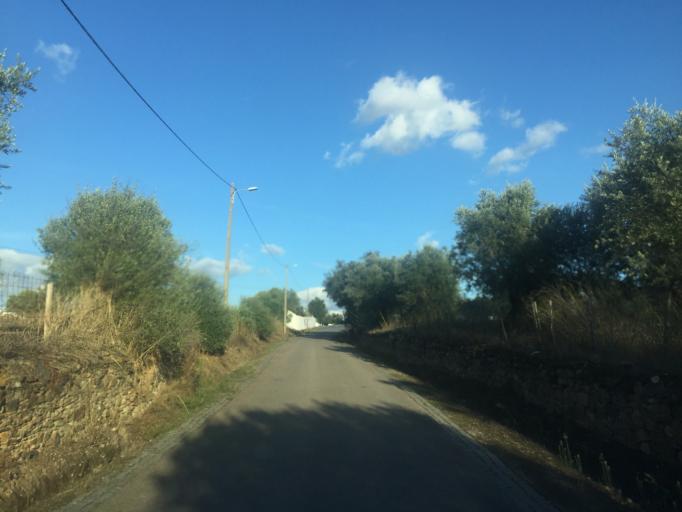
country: PT
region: Portalegre
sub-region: Alter do Chao
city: Alter do Chao
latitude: 39.1968
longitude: -7.6688
